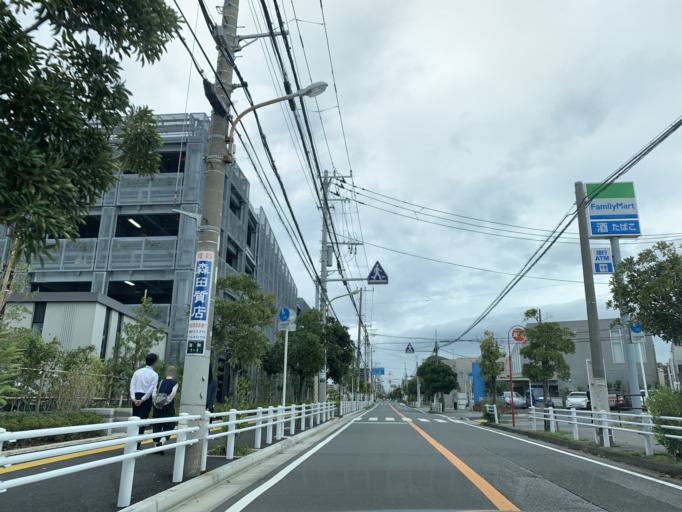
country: JP
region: Tokyo
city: Urayasu
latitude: 35.6536
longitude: 139.9027
